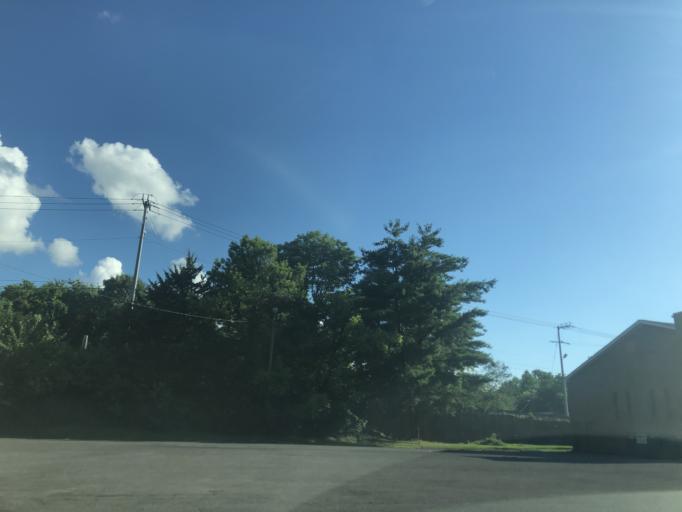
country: US
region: Tennessee
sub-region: Davidson County
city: Nashville
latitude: 36.1860
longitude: -86.7607
